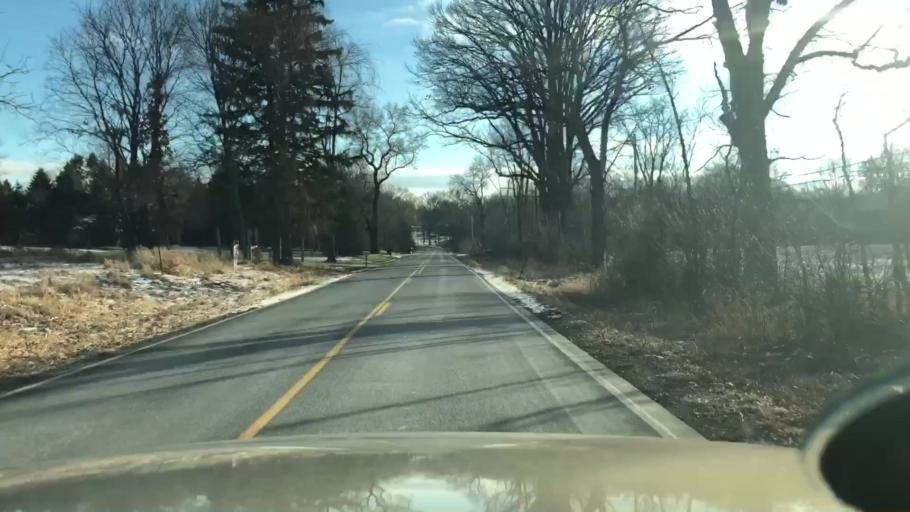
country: US
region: Michigan
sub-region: Jackson County
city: Vandercook Lake
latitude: 42.1642
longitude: -84.4524
